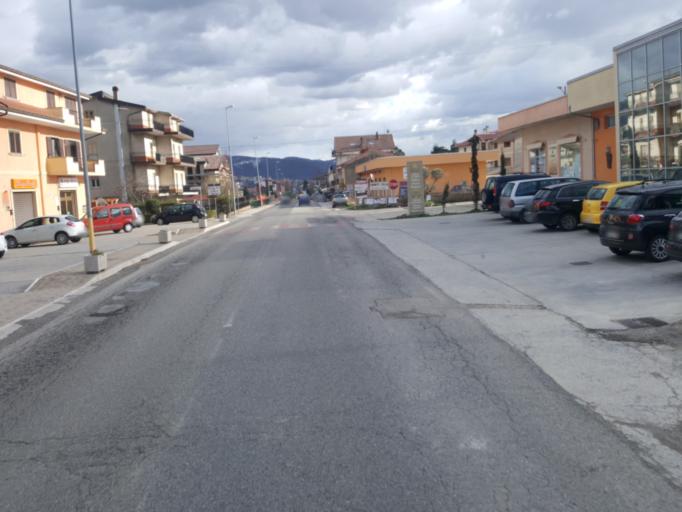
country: IT
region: Calabria
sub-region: Provincia di Cosenza
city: Santo Stefano di Rogliano
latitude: 39.2117
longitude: 16.3090
